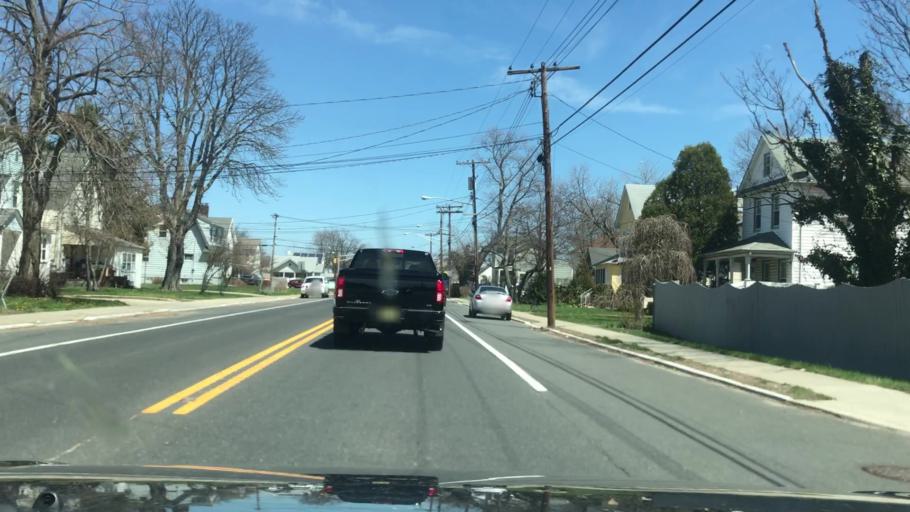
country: US
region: New Jersey
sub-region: Monmouth County
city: Long Branch
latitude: 40.3109
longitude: -73.9899
